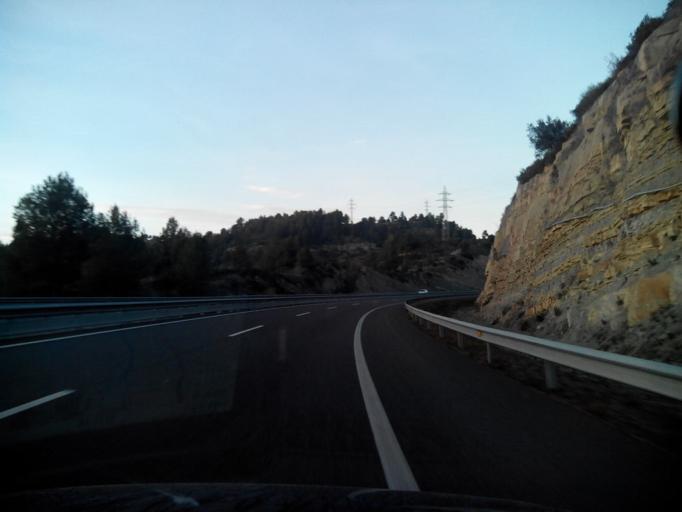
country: ES
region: Catalonia
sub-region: Provincia de Barcelona
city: Manresa
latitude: 41.6940
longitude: 1.8657
